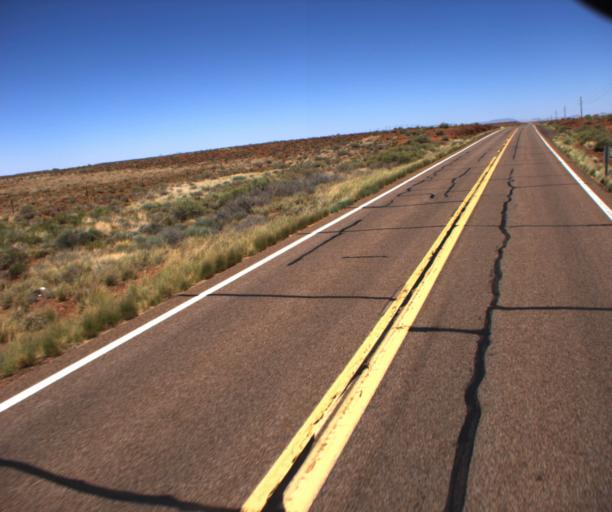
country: US
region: Arizona
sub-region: Coconino County
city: LeChee
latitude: 34.9183
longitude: -110.8235
